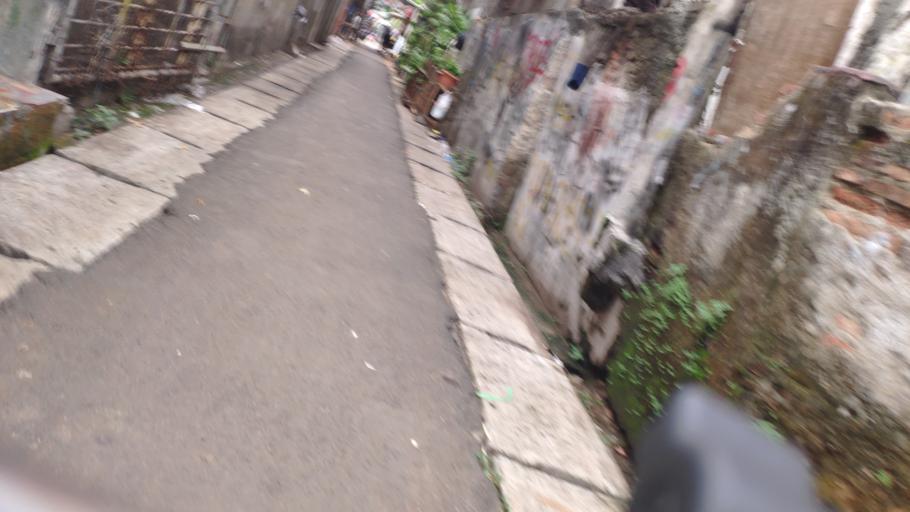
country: ID
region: Jakarta Raya
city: Jakarta
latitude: -6.2158
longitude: 106.8377
